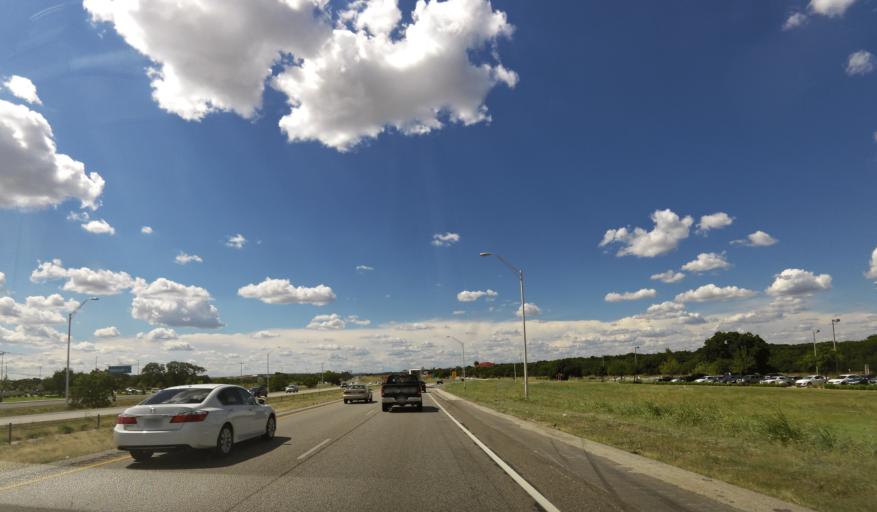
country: US
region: Texas
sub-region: Bexar County
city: Cross Mountain
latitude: 29.6686
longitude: -98.6323
